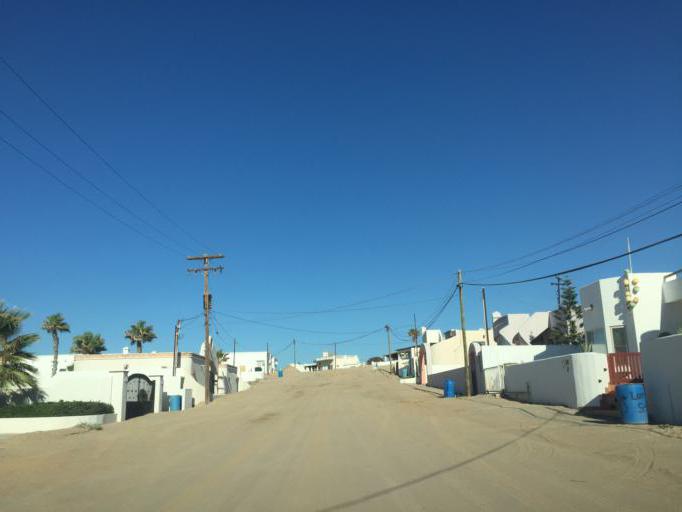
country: MX
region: Sonora
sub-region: Puerto Penasco
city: Puerto Penasco
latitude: 31.2885
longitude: -113.4845
